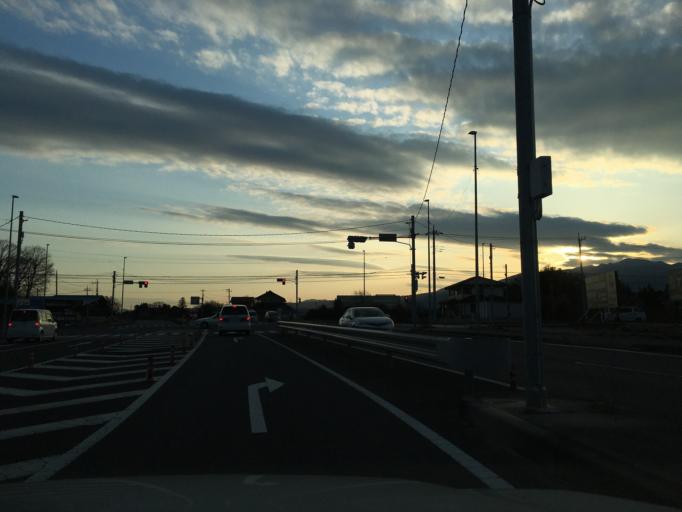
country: JP
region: Tochigi
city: Otawara
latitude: 36.9110
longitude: 139.9455
